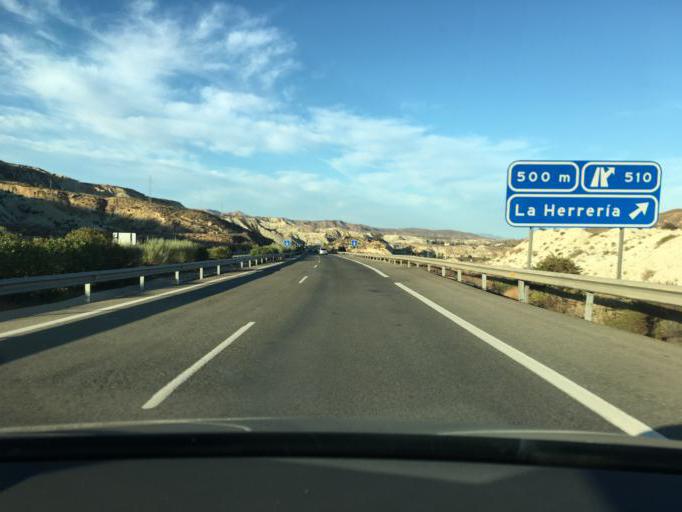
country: ES
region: Andalusia
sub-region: Provincia de Almeria
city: Sorbas
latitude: 37.1004
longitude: -2.0382
